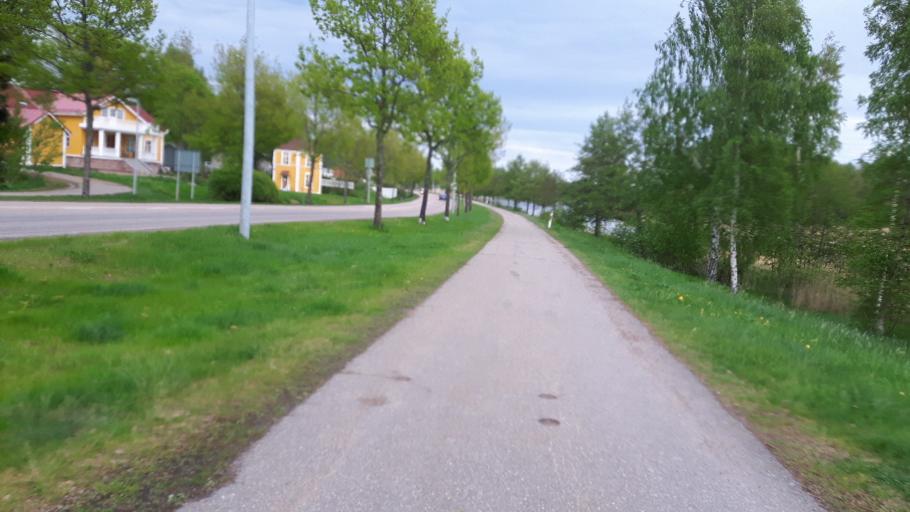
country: FI
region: Kymenlaakso
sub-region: Kotka-Hamina
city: Hamina
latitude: 60.5632
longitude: 27.2046
